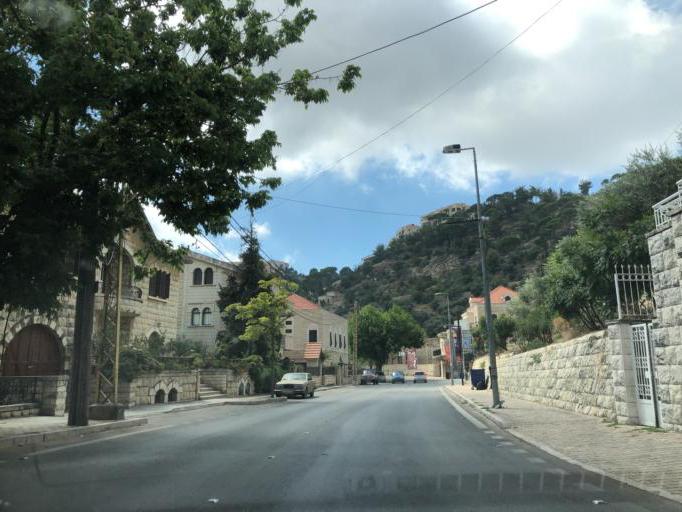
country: LB
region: Mont-Liban
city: Beit ed Dine
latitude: 33.6970
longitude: 35.5584
